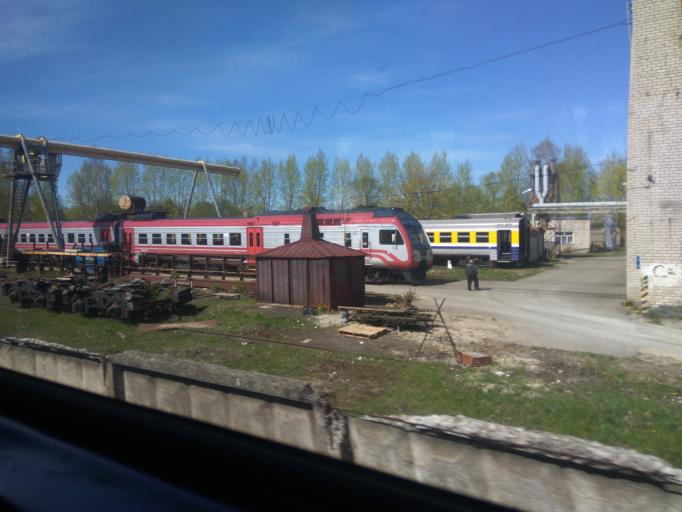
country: LV
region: Marupe
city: Marupe
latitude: 56.9473
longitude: 24.0348
